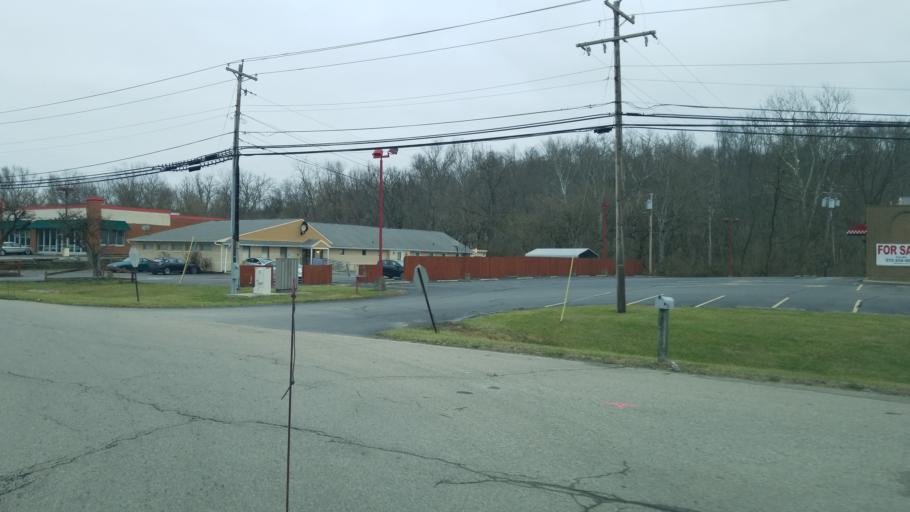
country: US
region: Ohio
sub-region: Clermont County
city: New Richmond
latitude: 38.9650
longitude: -84.2854
